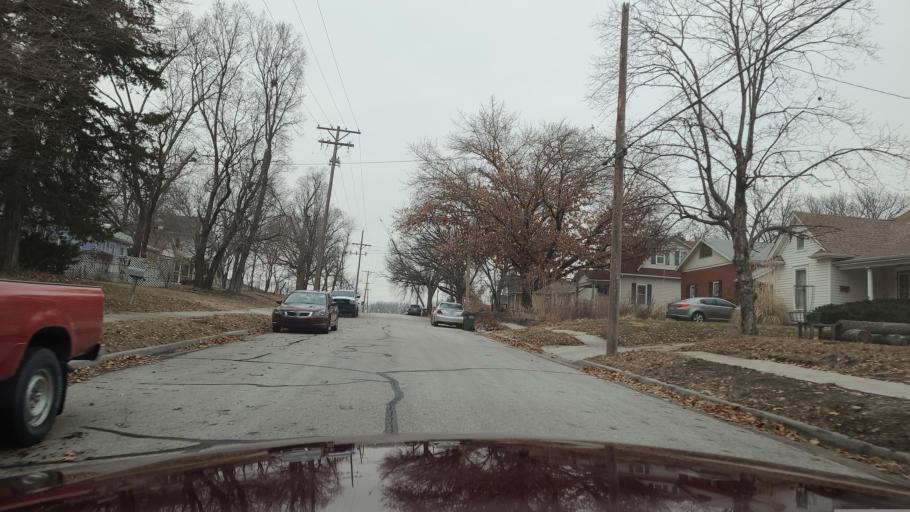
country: US
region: Kansas
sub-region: Douglas County
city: Lawrence
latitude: 38.9773
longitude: -95.2441
